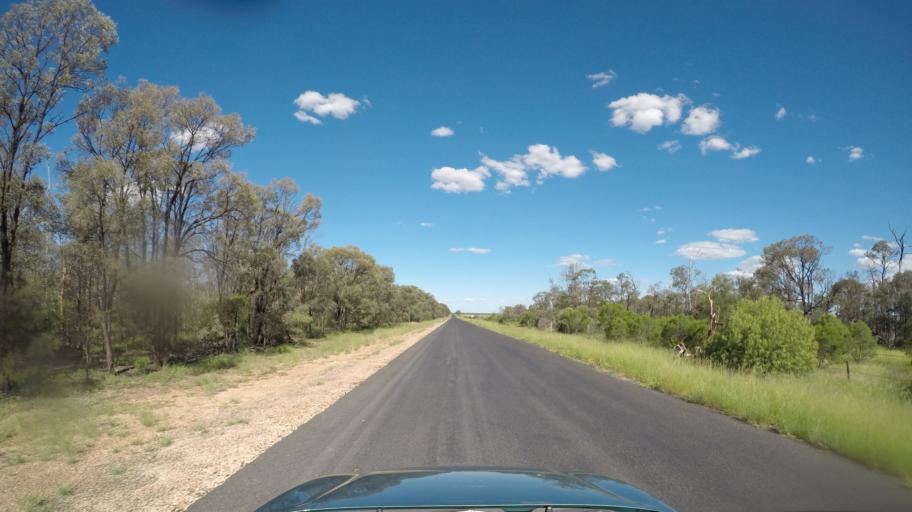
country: AU
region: Queensland
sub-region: Goondiwindi
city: Goondiwindi
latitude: -28.1618
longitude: 150.4137
